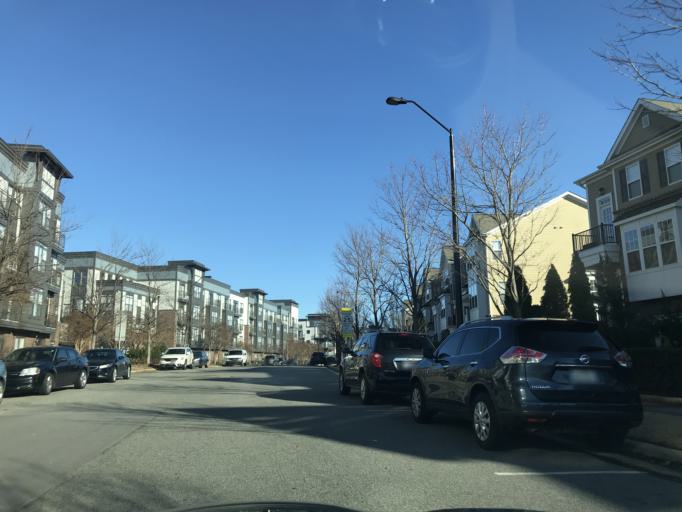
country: US
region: North Carolina
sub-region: Wake County
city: Morrisville
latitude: 35.9005
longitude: -78.8032
